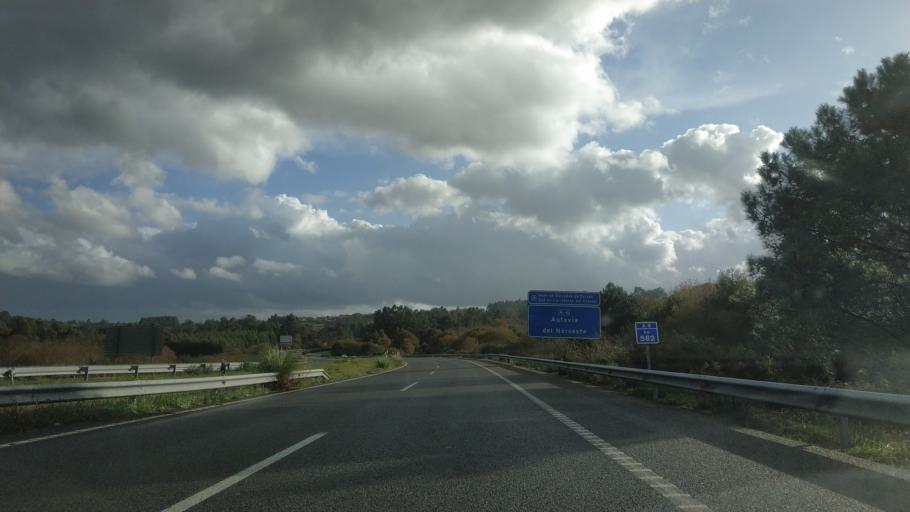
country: ES
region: Galicia
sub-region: Provincia da Coruna
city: Cambre
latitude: 43.2713
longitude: -8.3603
